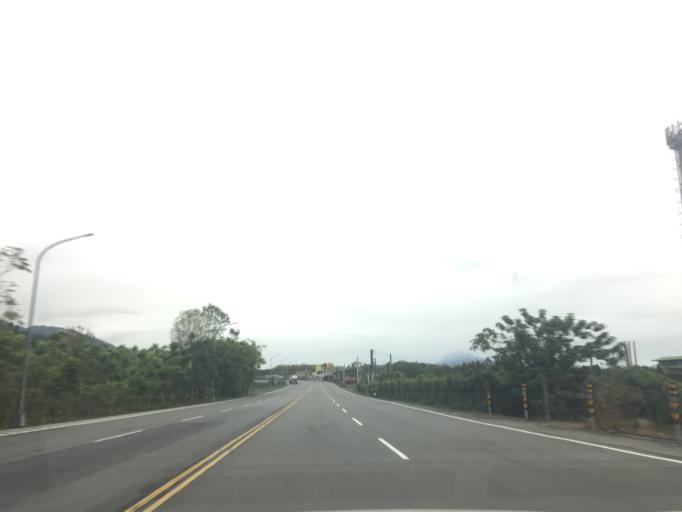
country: TW
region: Taiwan
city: Taitung City
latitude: 22.7241
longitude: 121.0552
